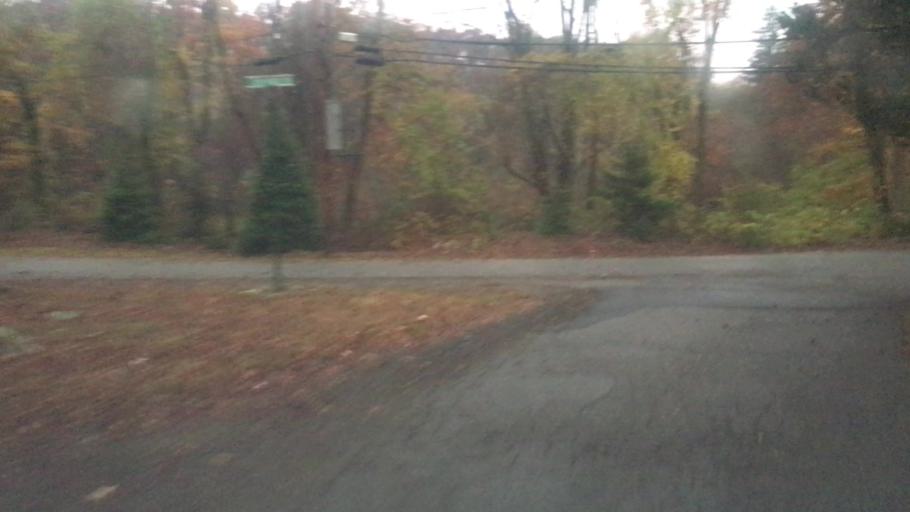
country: US
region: New Jersey
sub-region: Morris County
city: Butler
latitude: 41.0181
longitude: -74.3346
